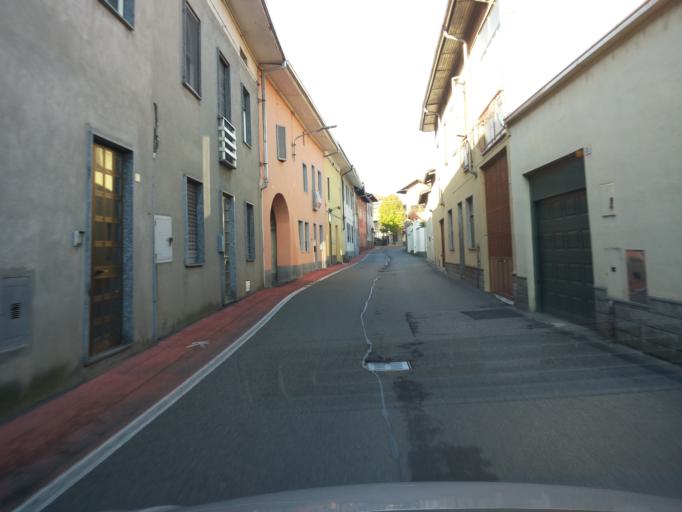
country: IT
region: Piedmont
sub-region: Provincia di Vercelli
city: Cigliano
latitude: 45.3062
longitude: 8.0168
